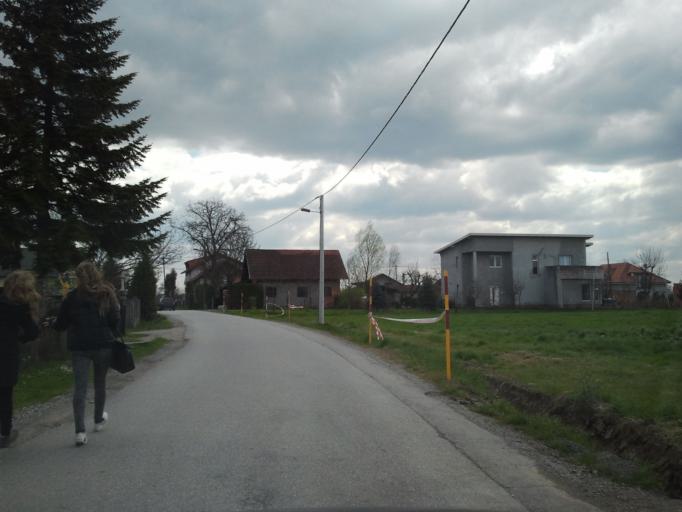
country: HR
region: Grad Zagreb
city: Brezovica
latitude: 45.7374
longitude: 15.8865
